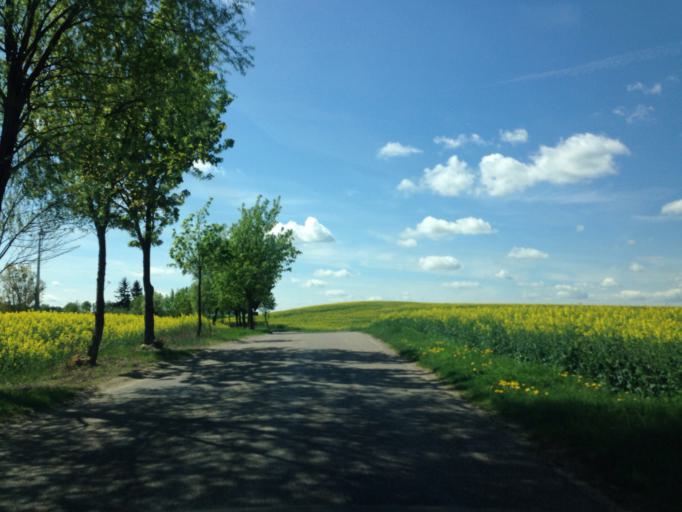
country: PL
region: Kujawsko-Pomorskie
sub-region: Powiat brodnicki
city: Brzozie
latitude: 53.2932
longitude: 19.6553
